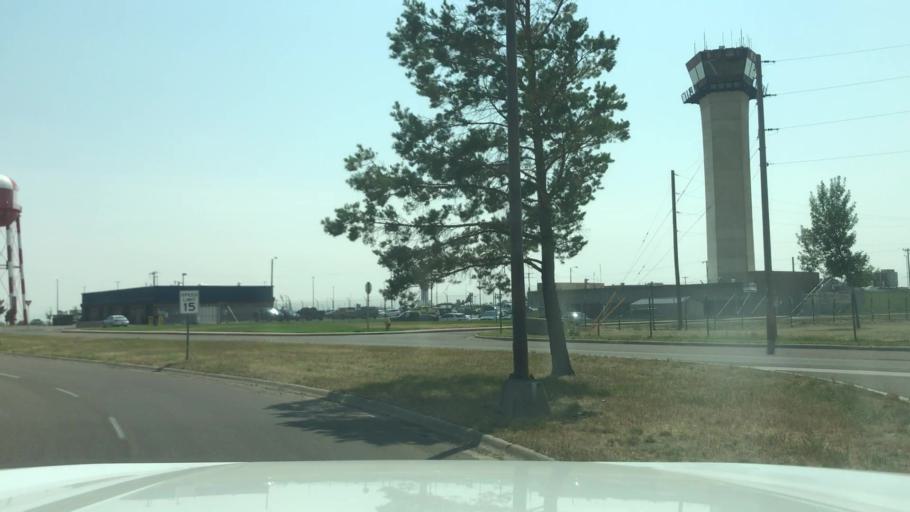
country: US
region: Montana
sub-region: Cascade County
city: Great Falls
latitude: 47.4812
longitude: -111.3594
